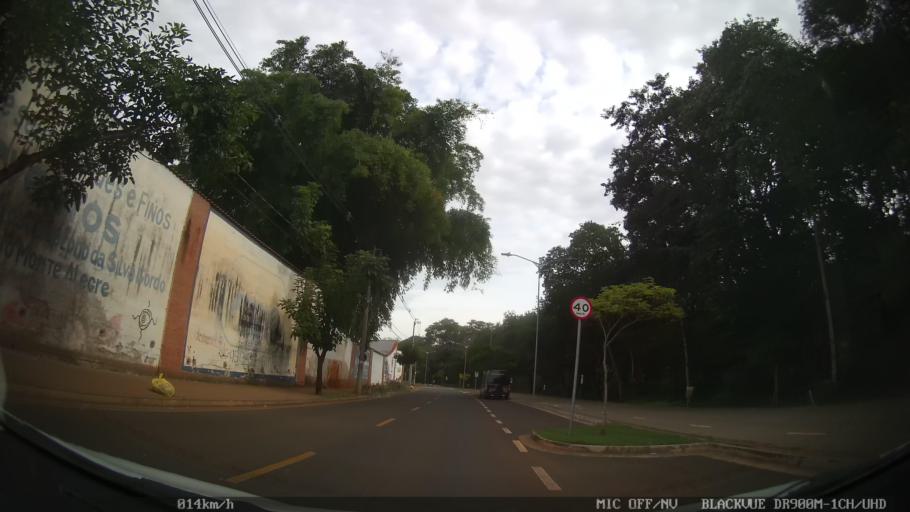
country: BR
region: Sao Paulo
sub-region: Piracicaba
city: Piracicaba
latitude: -22.7070
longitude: -47.6494
